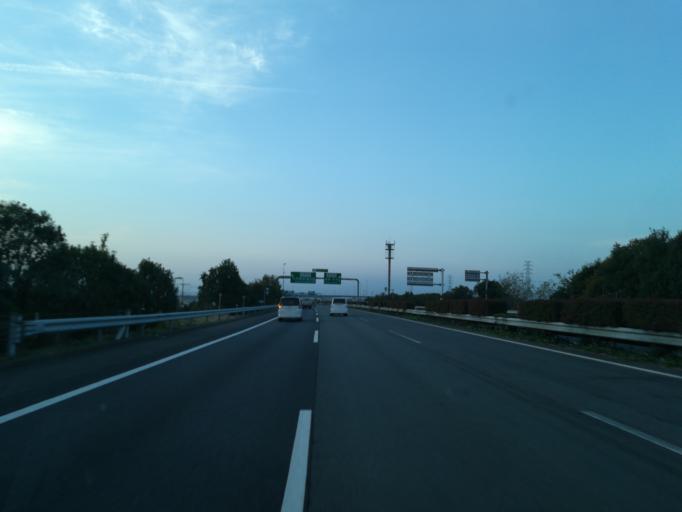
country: JP
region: Gunma
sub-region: Sawa-gun
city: Tamamura
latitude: 36.3170
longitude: 139.0815
